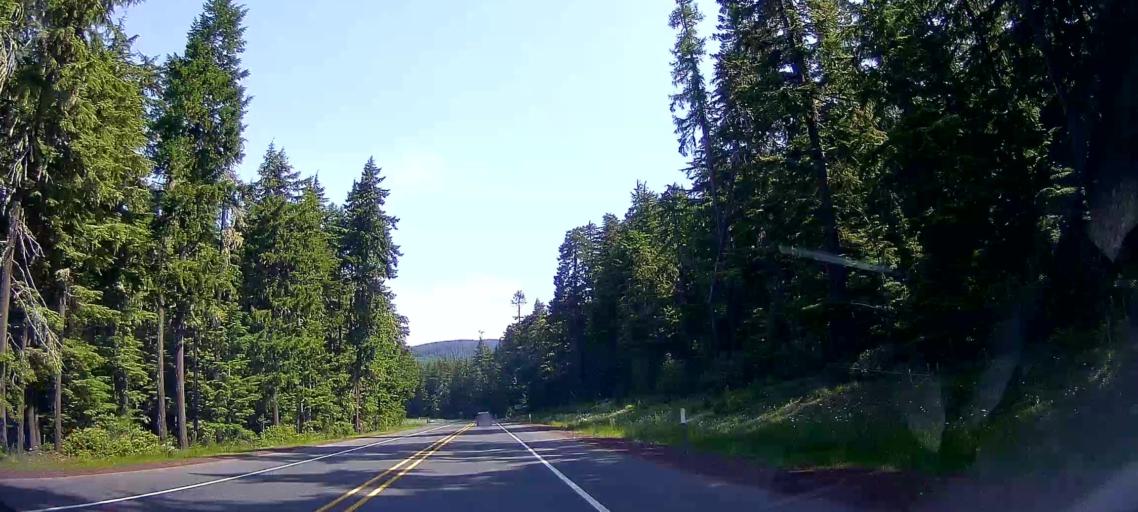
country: US
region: Oregon
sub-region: Clackamas County
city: Mount Hood Village
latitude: 45.1841
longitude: -121.6773
